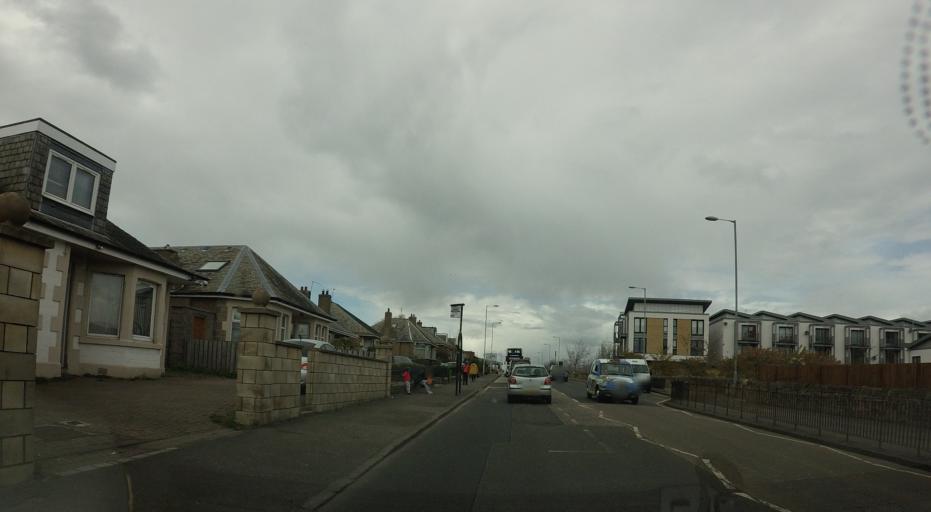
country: GB
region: Scotland
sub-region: Edinburgh
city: Edinburgh
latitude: 55.9663
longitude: -3.2346
